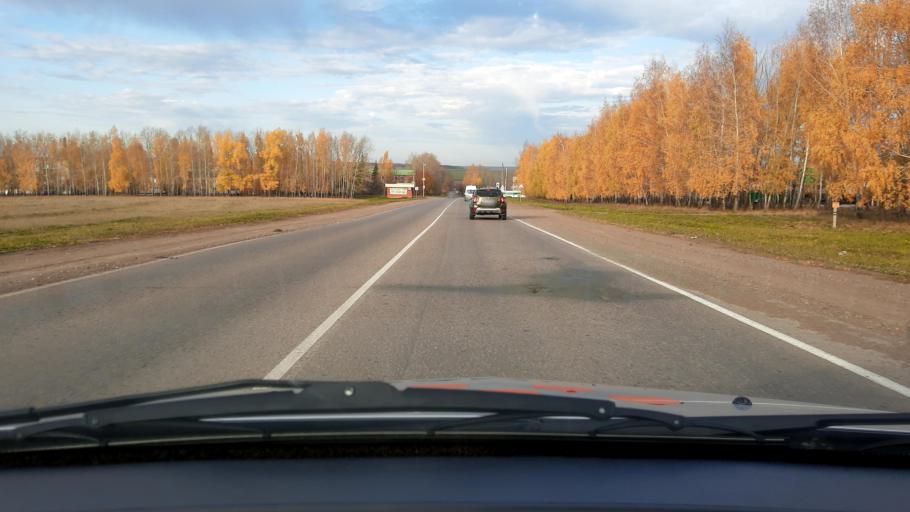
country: RU
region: Bashkortostan
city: Avdon
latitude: 54.8200
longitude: 55.7054
